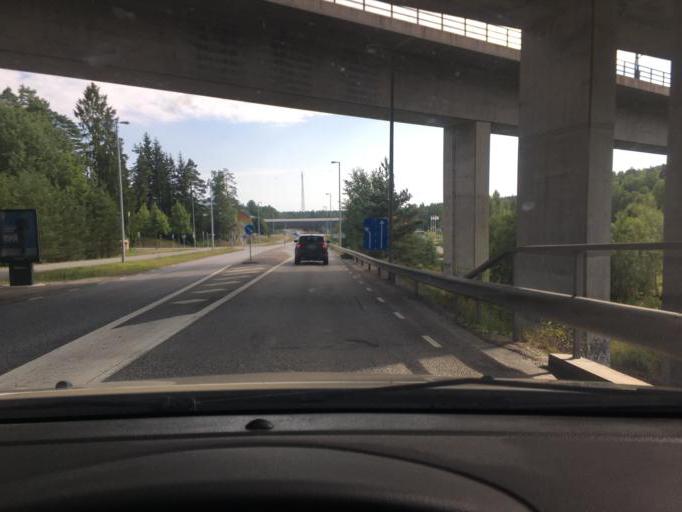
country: SE
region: Stockholm
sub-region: Sodertalje Kommun
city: Pershagen
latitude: 59.1614
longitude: 17.6420
